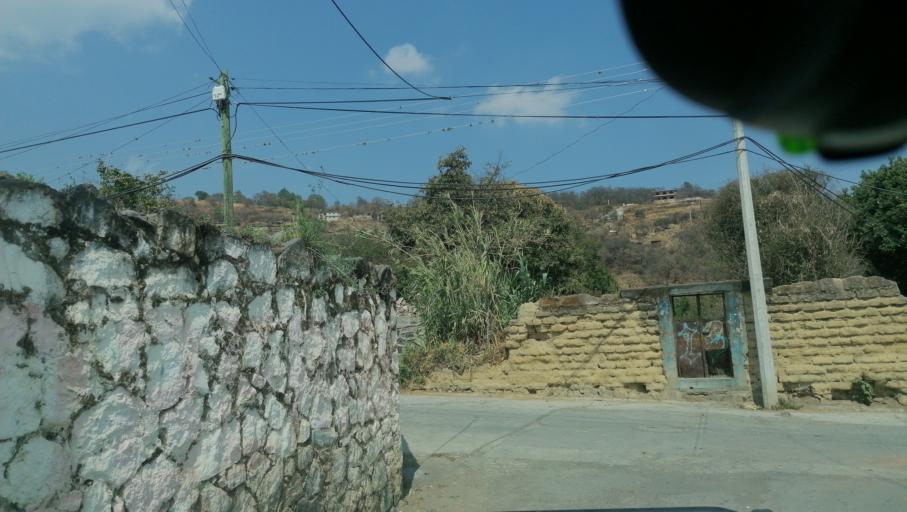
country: MX
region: Puebla
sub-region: Tochimilco
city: La Magdalena Yancuitlalpan
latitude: 18.9099
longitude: -98.5889
